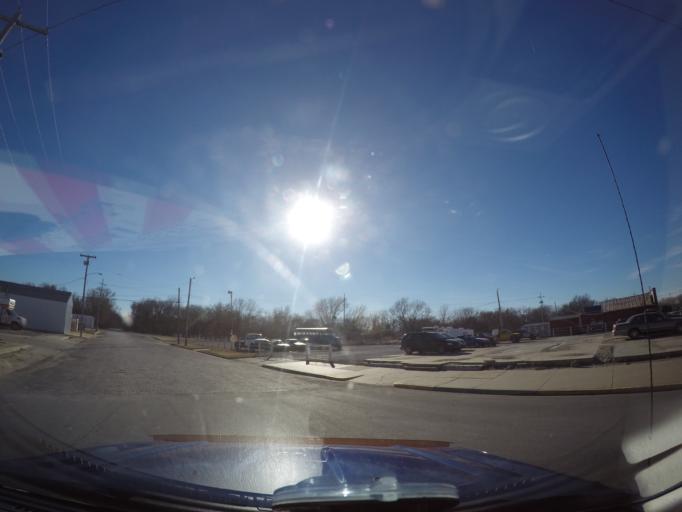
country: US
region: Kansas
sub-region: Marion County
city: Marion
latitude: 38.3481
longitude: -97.0219
